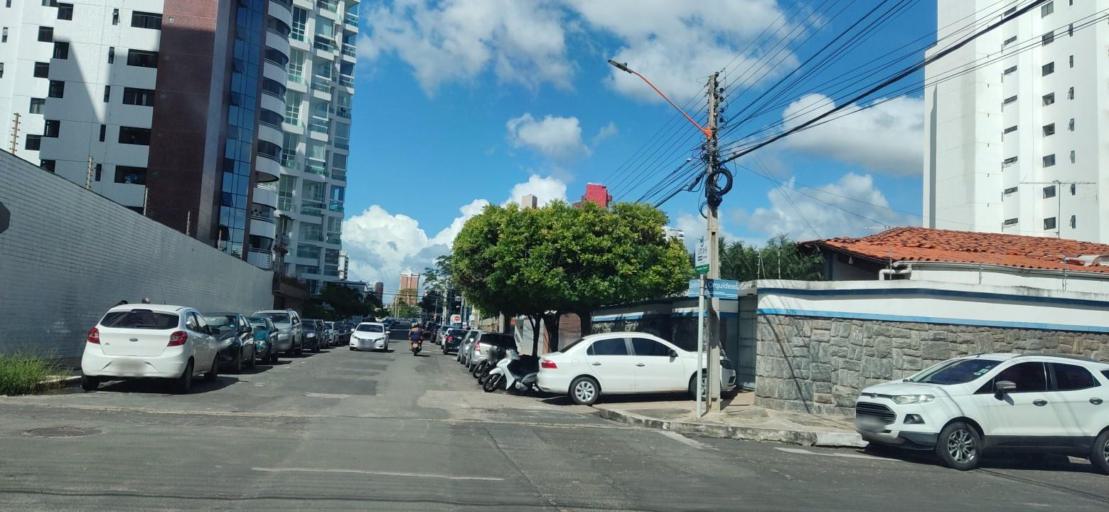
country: BR
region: Piaui
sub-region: Teresina
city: Teresina
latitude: -5.0778
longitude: -42.7922
